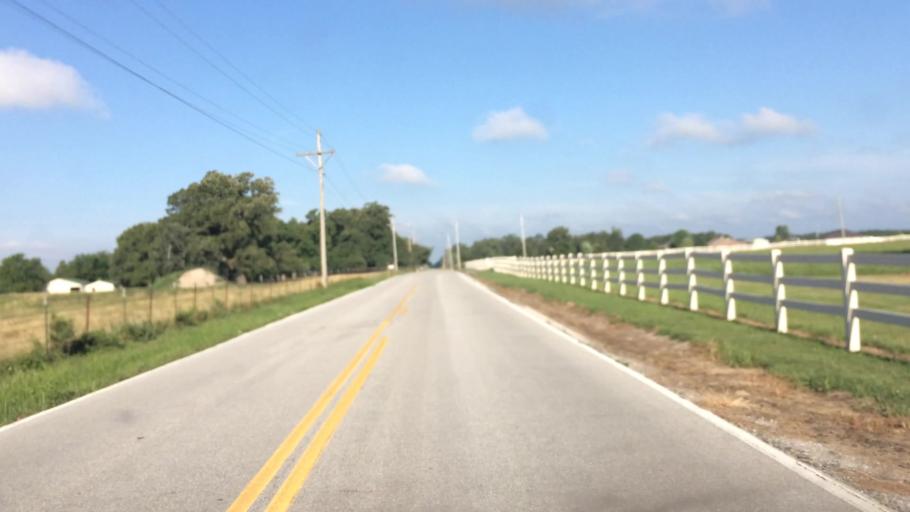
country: US
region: Missouri
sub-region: Greene County
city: Strafford
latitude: 37.2714
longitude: -93.1595
